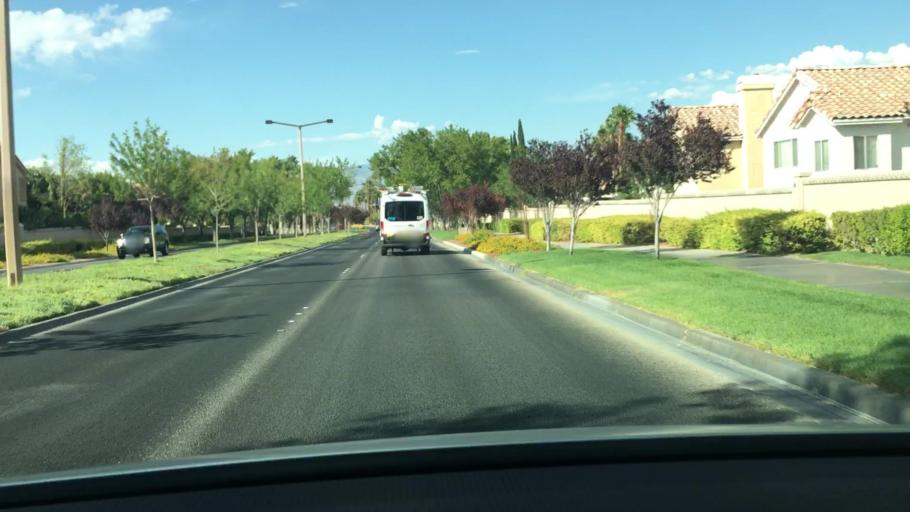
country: US
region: Nevada
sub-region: Clark County
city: Summerlin South
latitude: 36.2035
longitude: -115.3002
